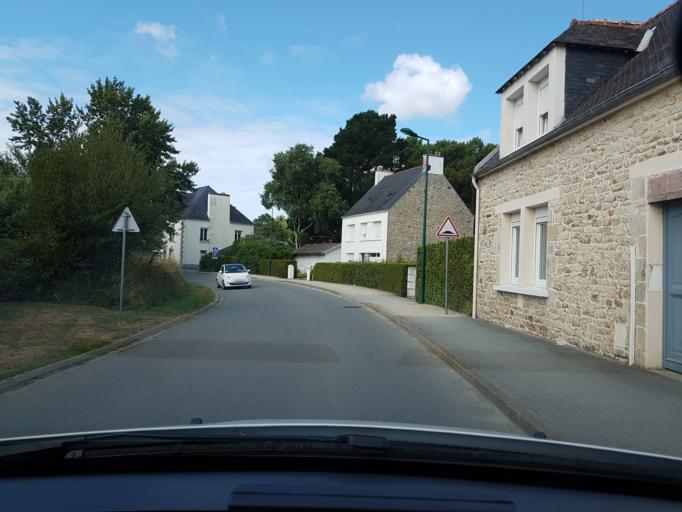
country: FR
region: Brittany
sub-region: Departement du Morbihan
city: Sainte-Helene
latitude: 47.7195
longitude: -3.2073
